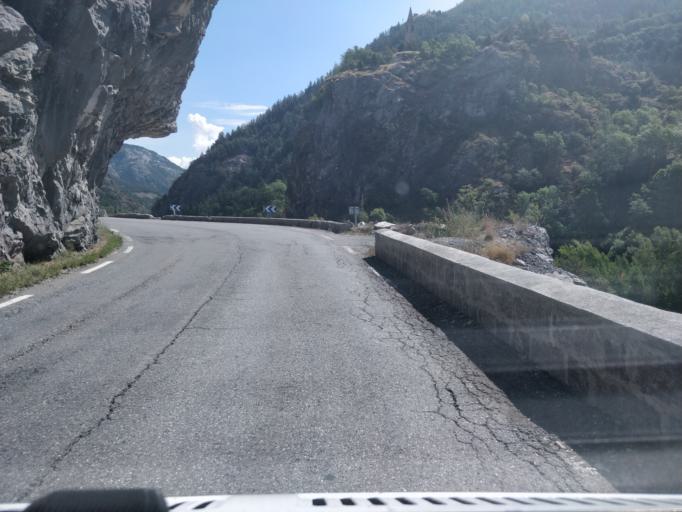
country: FR
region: Provence-Alpes-Cote d'Azur
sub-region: Departement des Alpes-de-Haute-Provence
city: Barcelonnette
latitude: 44.3998
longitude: 6.5038
